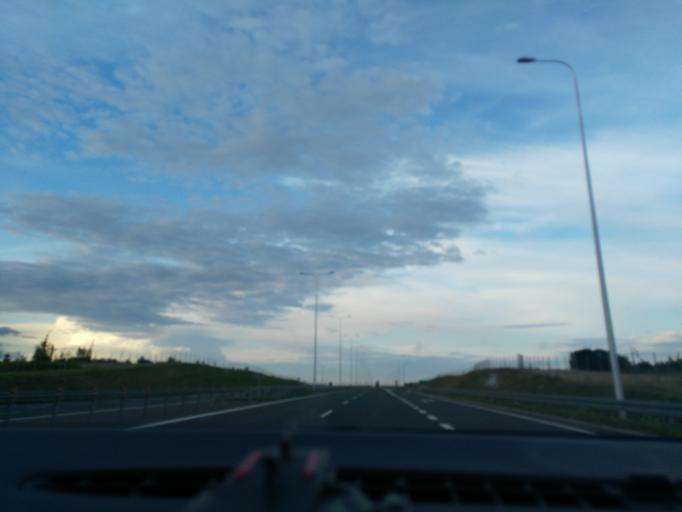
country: PL
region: Lublin Voivodeship
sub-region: Powiat lubelski
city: Jastkow
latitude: 51.2791
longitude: 22.4421
